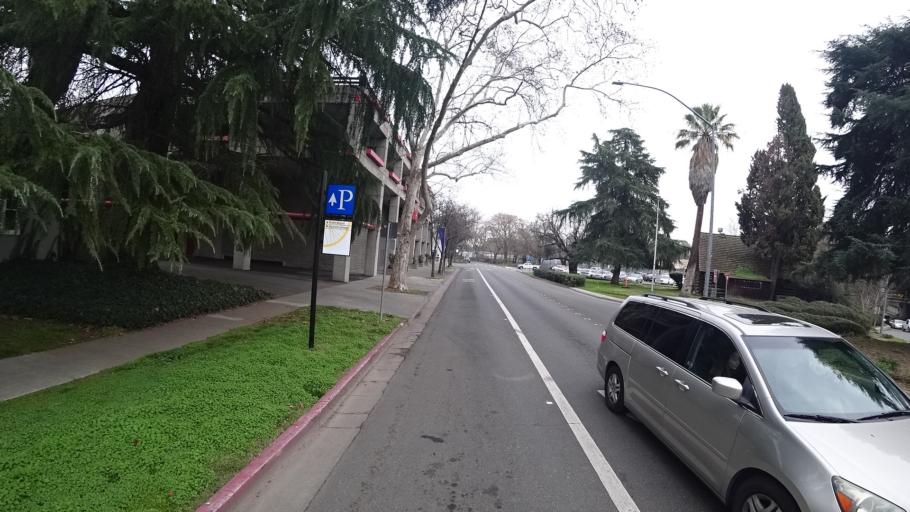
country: US
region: California
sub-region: Yolo County
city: Davis
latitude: 38.5421
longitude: -121.7405
